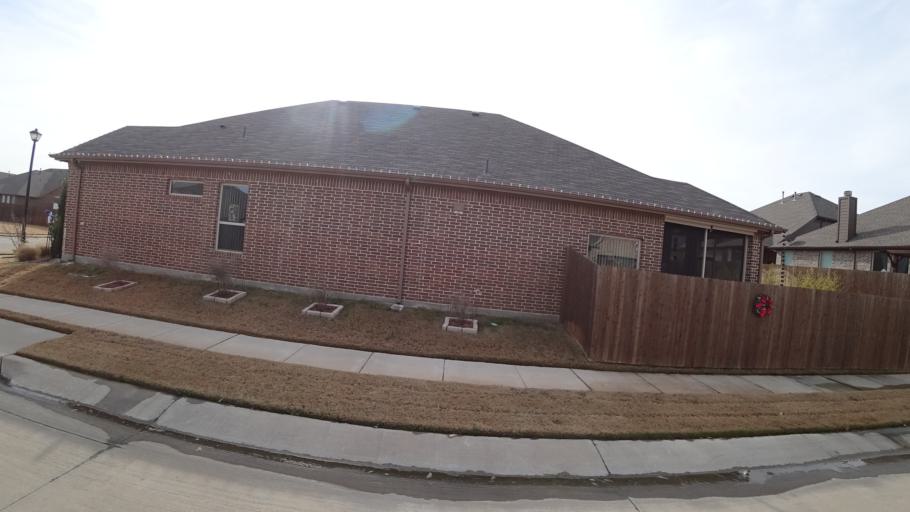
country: US
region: Texas
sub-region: Denton County
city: Highland Village
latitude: 33.0760
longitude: -97.0289
